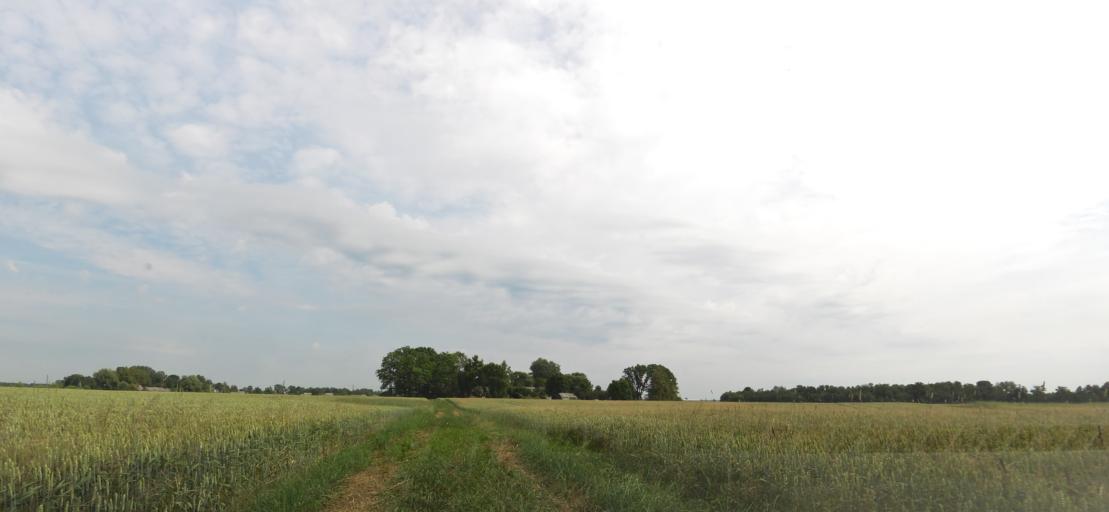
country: LT
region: Panevezys
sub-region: Birzai
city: Birzai
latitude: 56.3196
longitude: 24.6974
